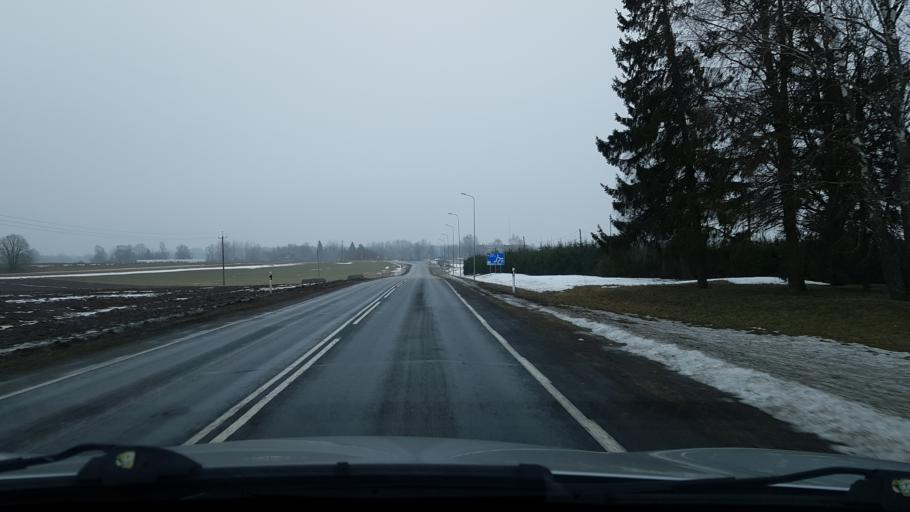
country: EE
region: Viljandimaa
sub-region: Viiratsi vald
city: Viiratsi
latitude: 58.2470
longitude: 25.8483
